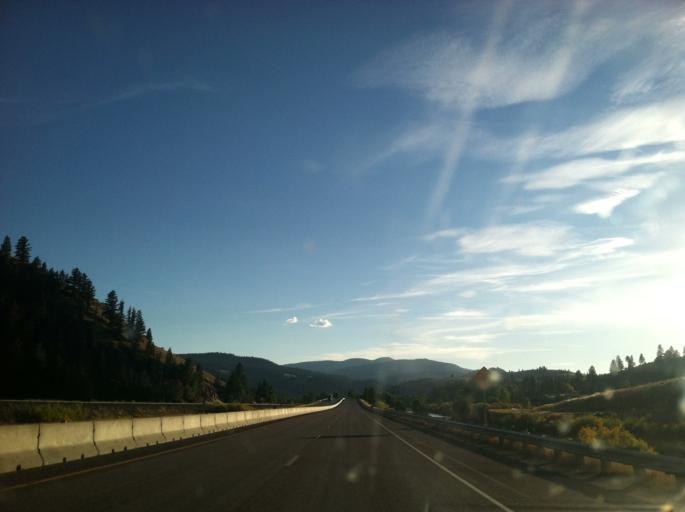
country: US
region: Montana
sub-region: Granite County
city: Philipsburg
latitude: 46.7148
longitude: -113.3251
